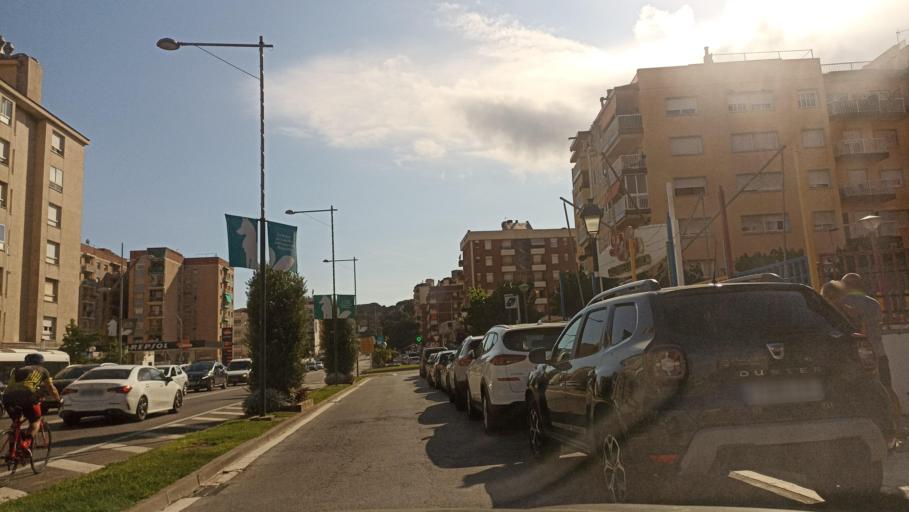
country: ES
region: Catalonia
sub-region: Provincia de Barcelona
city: Calella
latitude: 41.6134
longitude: 2.6531
